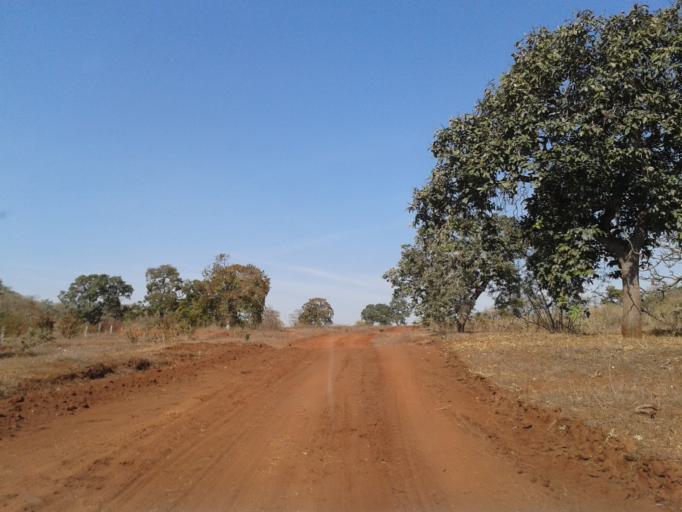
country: BR
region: Minas Gerais
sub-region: Santa Vitoria
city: Santa Vitoria
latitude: -19.2211
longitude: -50.0436
